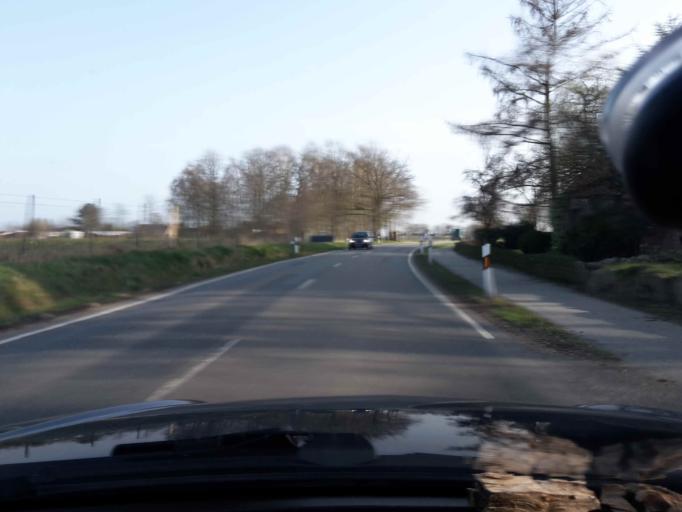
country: DE
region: Lower Saxony
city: Buxtehude
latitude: 53.4364
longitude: 9.6931
